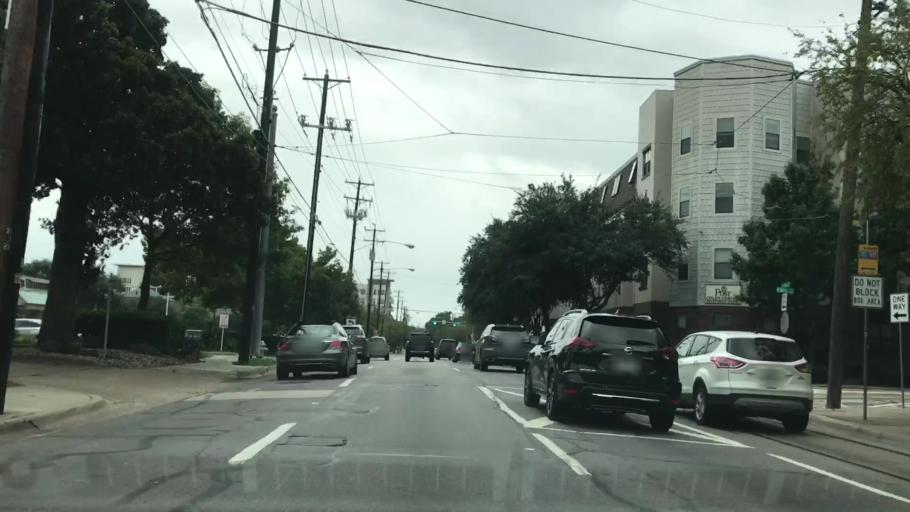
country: US
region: Texas
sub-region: Dallas County
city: Dallas
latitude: 32.8068
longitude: -96.7995
